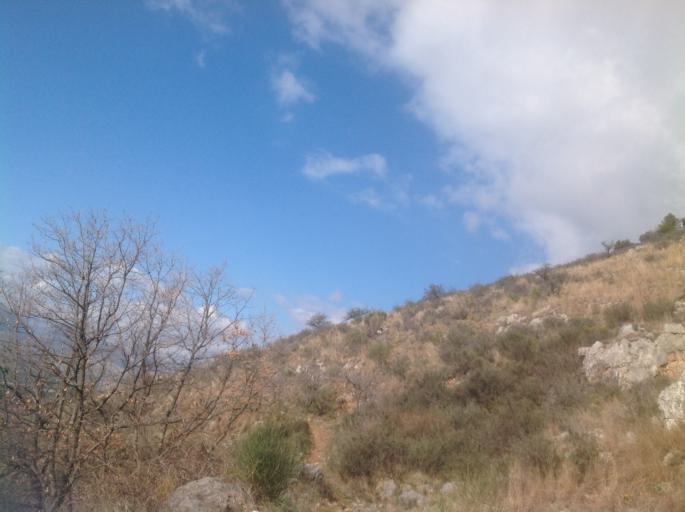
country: IT
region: Calabria
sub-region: Provincia di Cosenza
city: Frascineto
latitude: 39.8462
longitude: 16.2597
